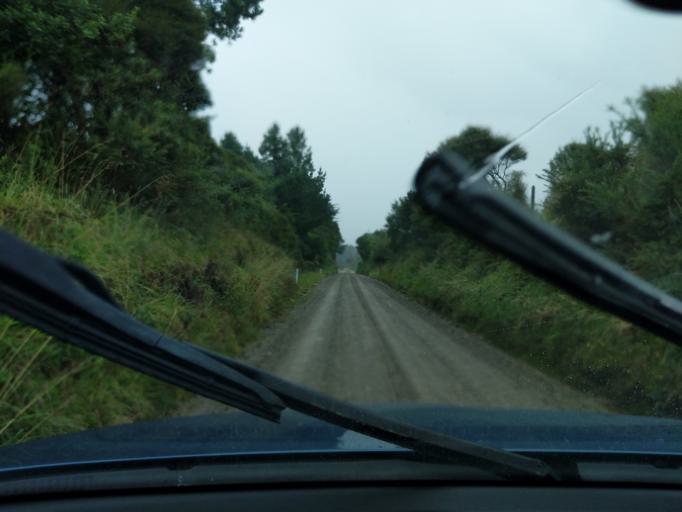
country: NZ
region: Tasman
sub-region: Tasman District
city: Takaka
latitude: -40.6327
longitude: 172.4903
